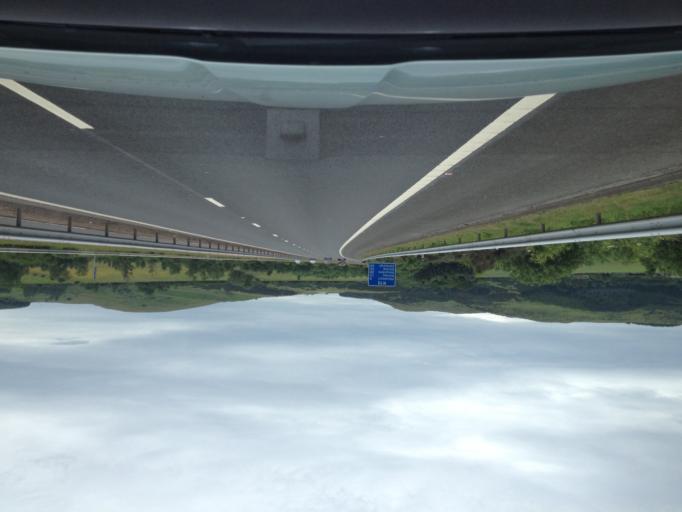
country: GB
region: Scotland
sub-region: Perth and Kinross
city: Bridge of Earn
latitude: 56.3351
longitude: -3.3996
